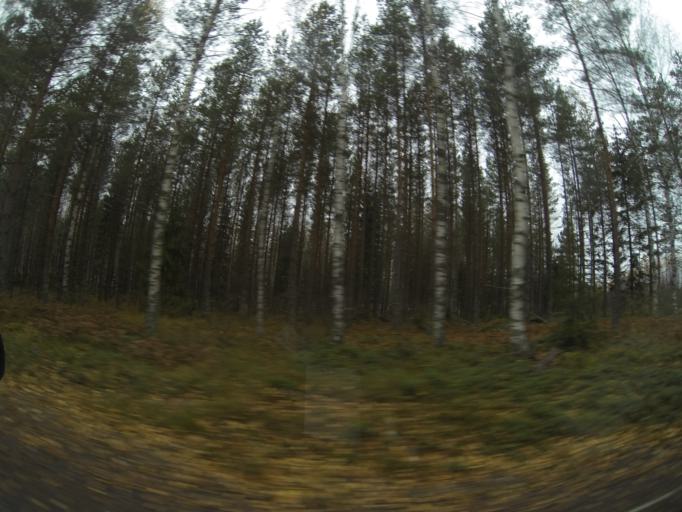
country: SE
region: Vaestmanland
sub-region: Surahammars Kommun
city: Surahammar
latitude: 59.6614
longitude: 16.0822
